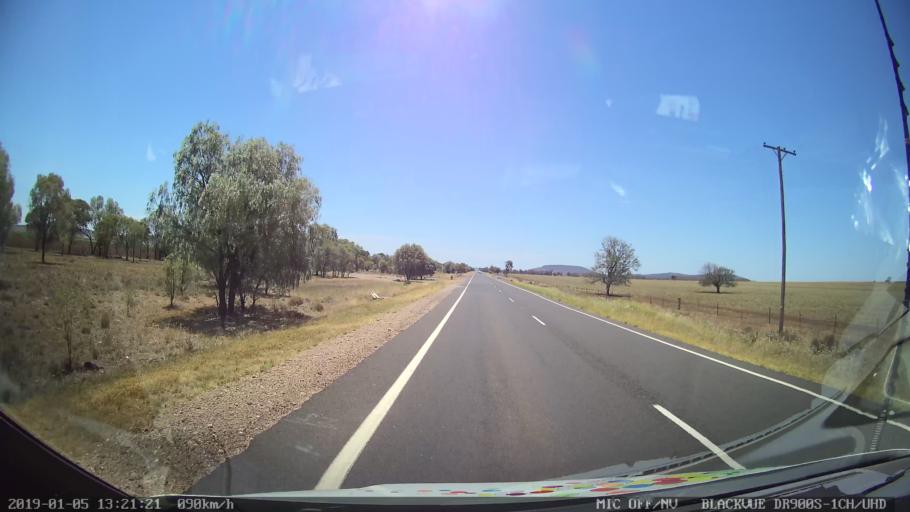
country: AU
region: New South Wales
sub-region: Gunnedah
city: Gunnedah
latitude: -31.0950
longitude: 149.9476
